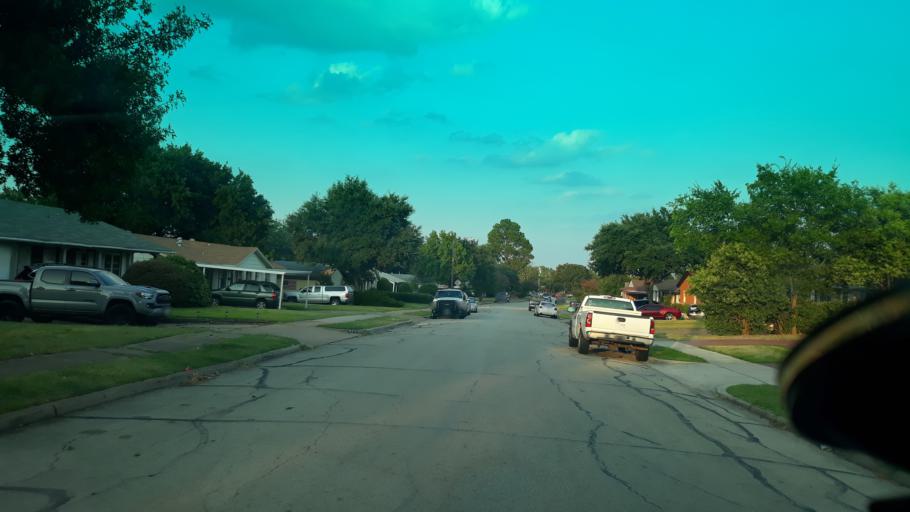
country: US
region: Texas
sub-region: Dallas County
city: Irving
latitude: 32.8396
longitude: -96.9821
